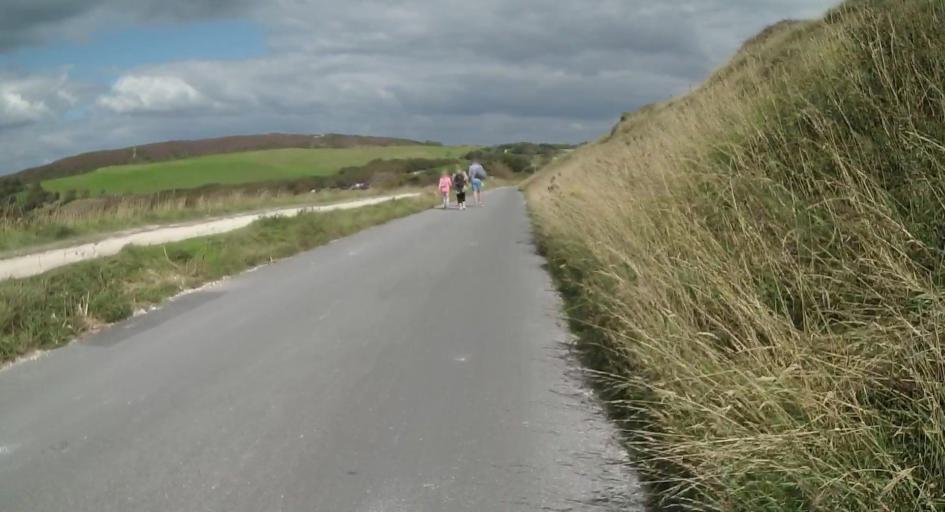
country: GB
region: England
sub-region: Isle of Wight
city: Totland
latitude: 50.6655
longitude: -1.5682
